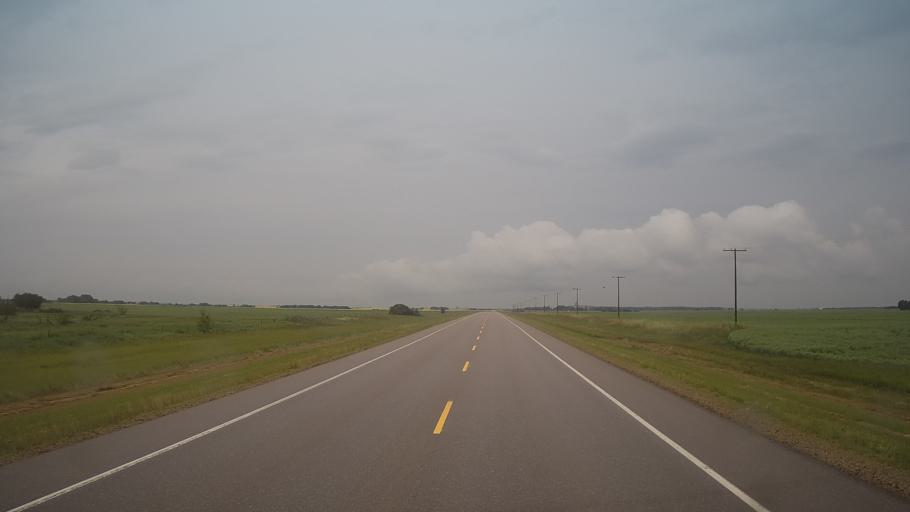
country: CA
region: Saskatchewan
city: Wilkie
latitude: 52.3212
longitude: -108.7030
